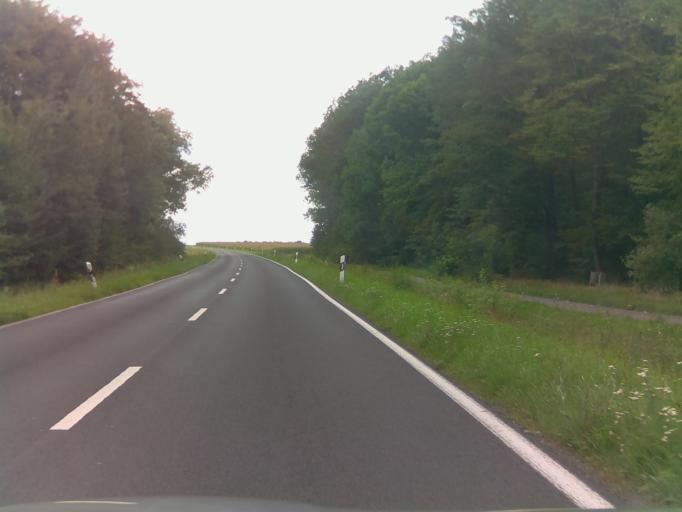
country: DE
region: Bavaria
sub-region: Regierungsbezirk Unterfranken
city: Grettstadt
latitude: 49.9866
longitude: 10.3421
